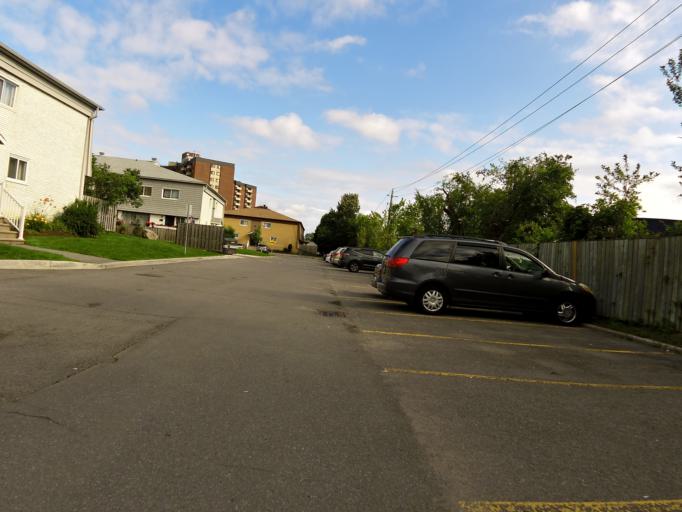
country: CA
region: Ontario
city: Bells Corners
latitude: 45.3518
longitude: -75.8052
